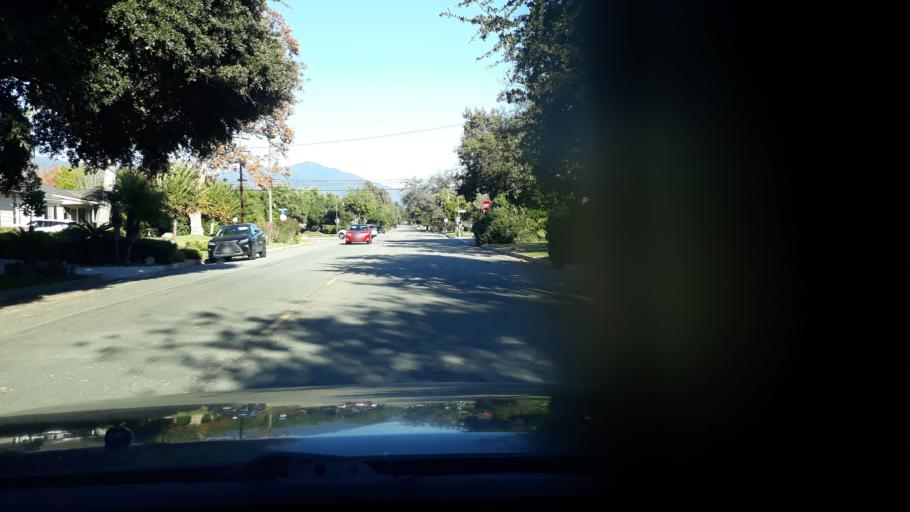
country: US
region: California
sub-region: Los Angeles County
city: San Marino
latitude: 34.1174
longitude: -118.1007
